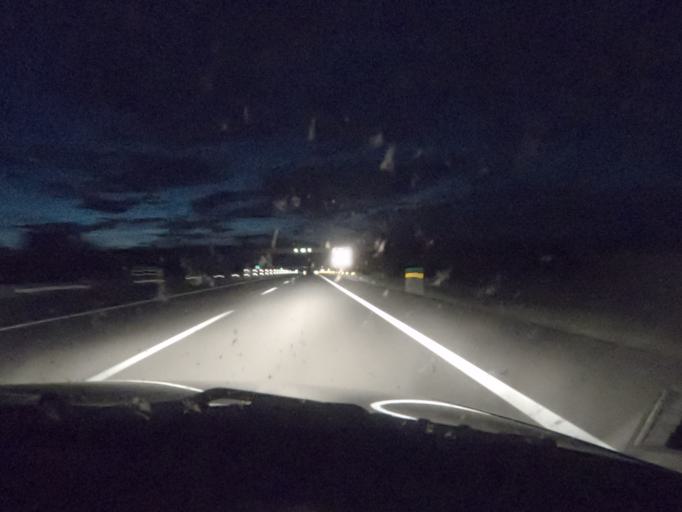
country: ES
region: Extremadura
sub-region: Provincia de Caceres
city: Casas de Don Gomez
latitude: 40.0159
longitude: -6.5846
